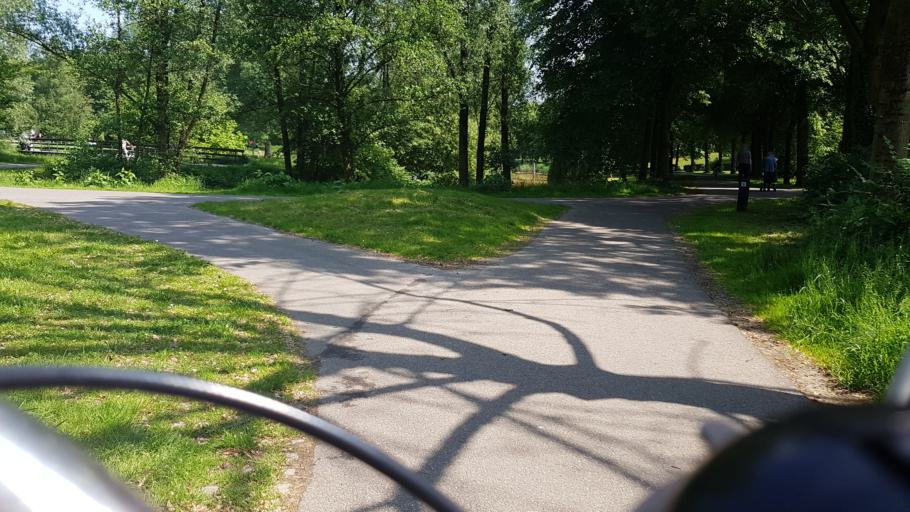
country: NL
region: Gelderland
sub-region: Gemeente Apeldoorn
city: Apeldoorn
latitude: 52.1949
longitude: 5.9974
